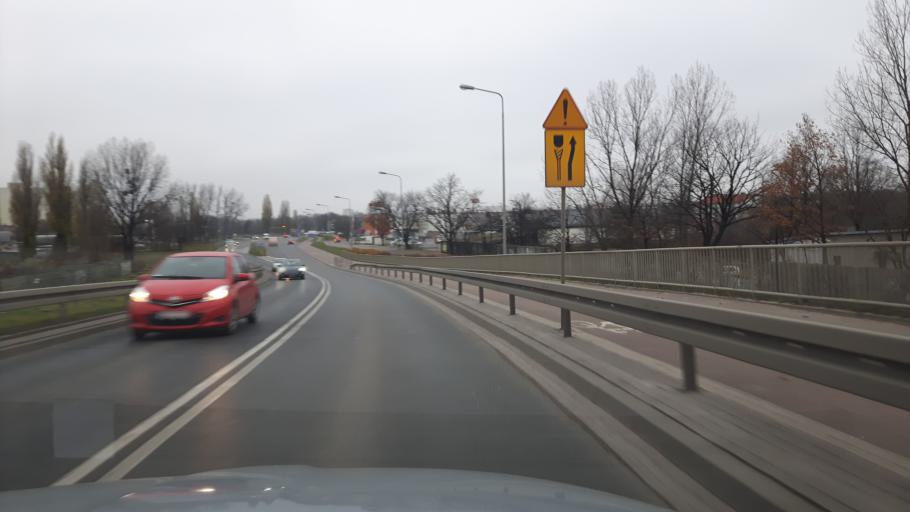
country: PL
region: Masovian Voivodeship
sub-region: Warszawa
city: Targowek
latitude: 52.2719
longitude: 21.0696
